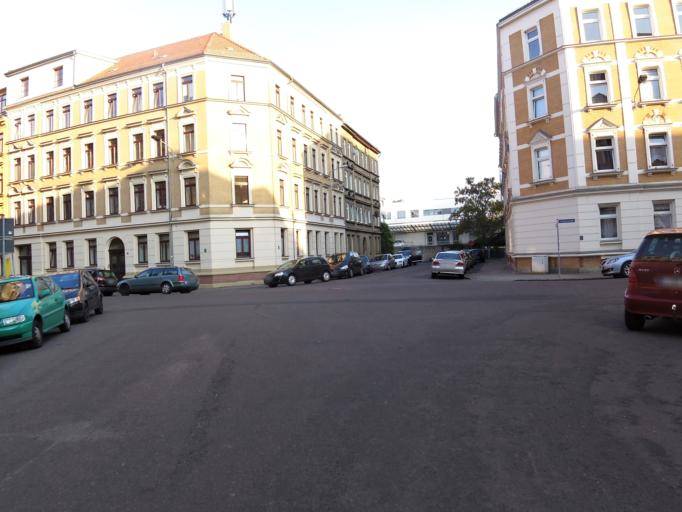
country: DE
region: Saxony
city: Leipzig
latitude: 51.3438
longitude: 12.3188
